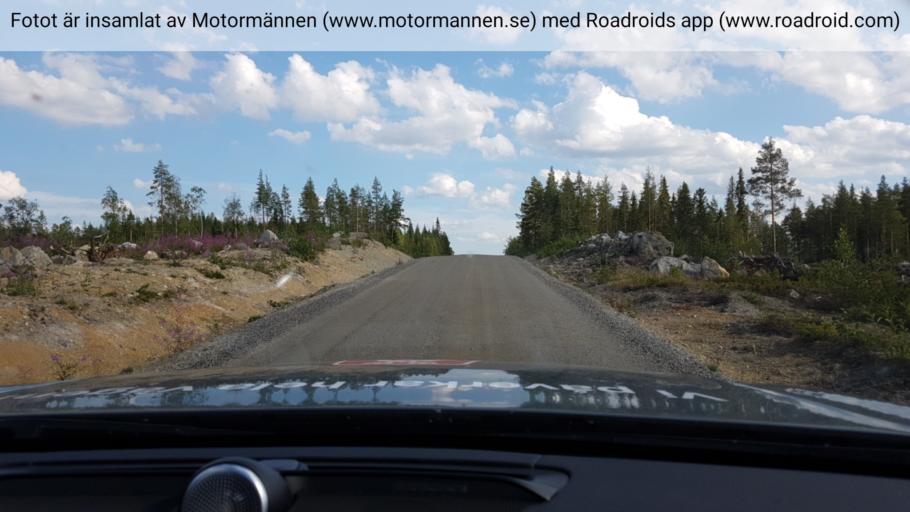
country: SE
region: Vaesterbotten
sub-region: Dorotea Kommun
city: Dorotea
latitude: 63.9399
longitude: 16.0899
